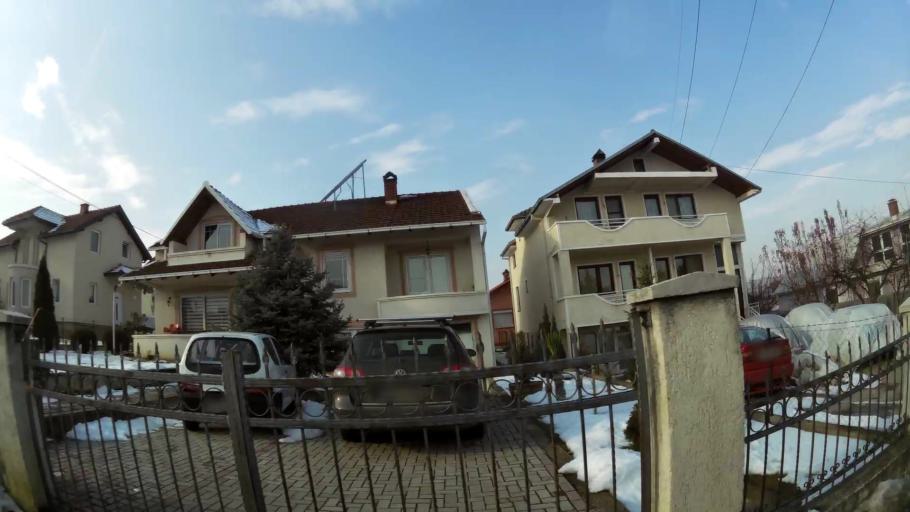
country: MK
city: Creshevo
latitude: 42.0101
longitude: 21.4974
